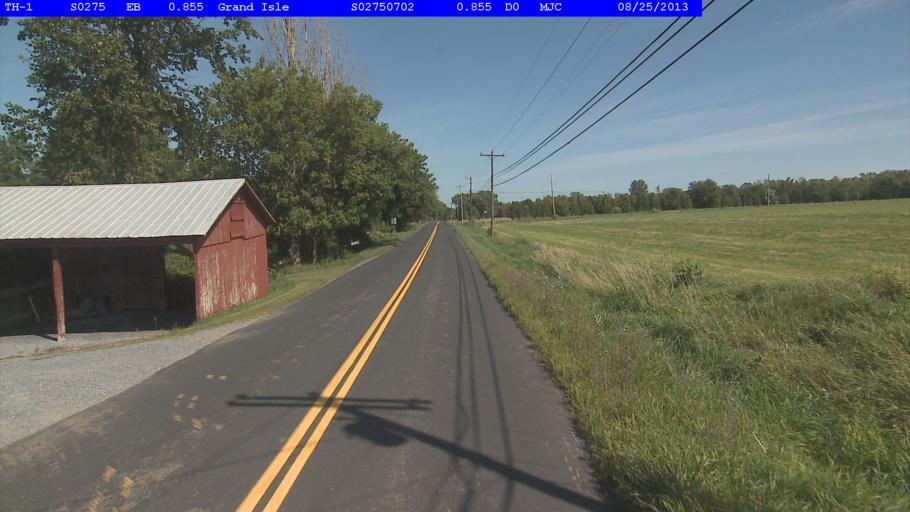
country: US
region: New York
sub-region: Clinton County
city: Cumberland Head
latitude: 44.7127
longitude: -73.3421
